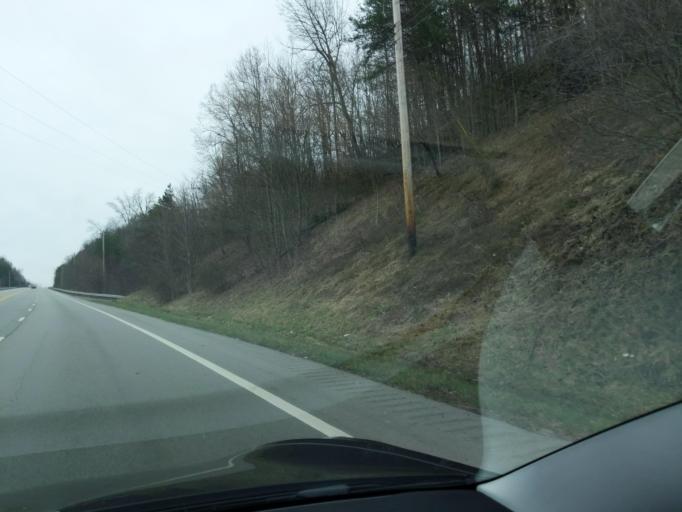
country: US
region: Kentucky
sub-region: Whitley County
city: Corbin
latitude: 36.9188
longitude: -84.1124
